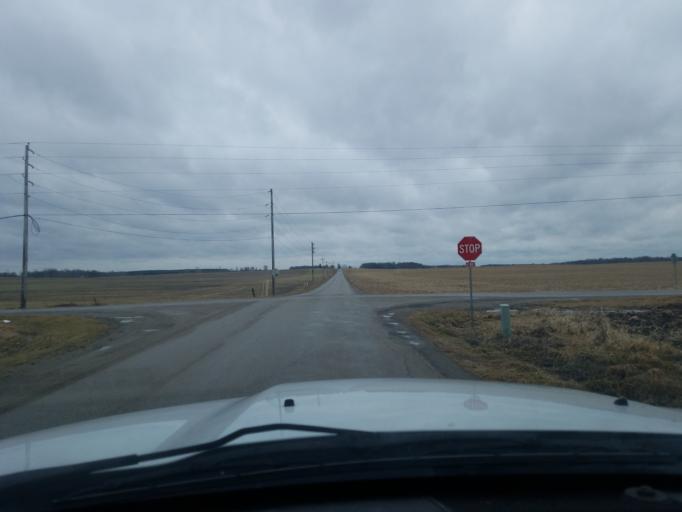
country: US
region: Indiana
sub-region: Noble County
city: Albion
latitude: 41.4387
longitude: -85.3946
